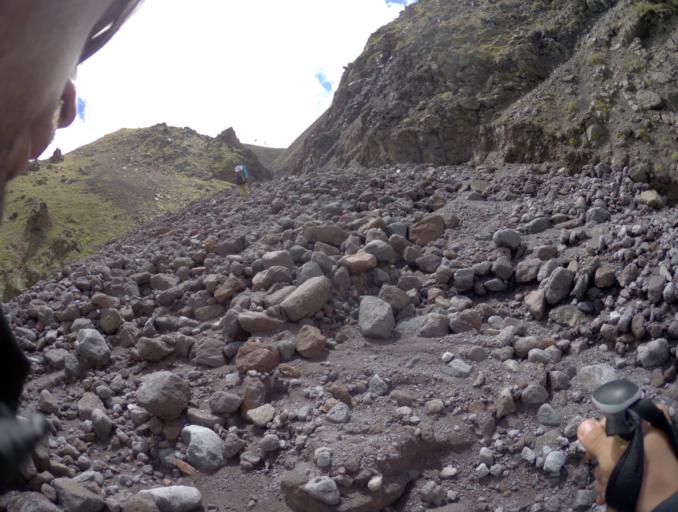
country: RU
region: Kabardino-Balkariya
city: Terskol
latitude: 43.3853
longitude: 42.3664
